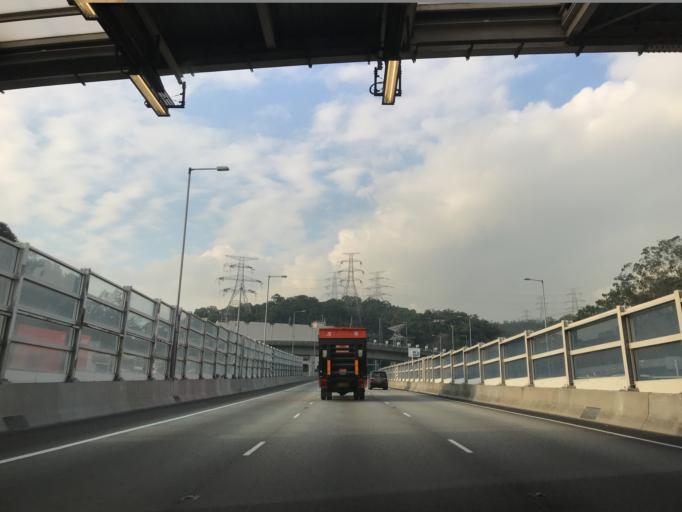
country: HK
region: Sham Shui Po
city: Sham Shui Po
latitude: 22.3387
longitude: 114.1444
